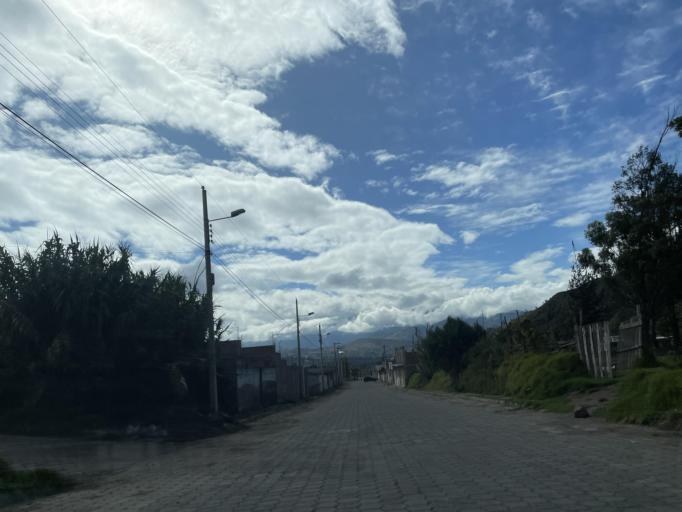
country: EC
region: Chimborazo
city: Guano
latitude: -1.6087
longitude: -78.6303
